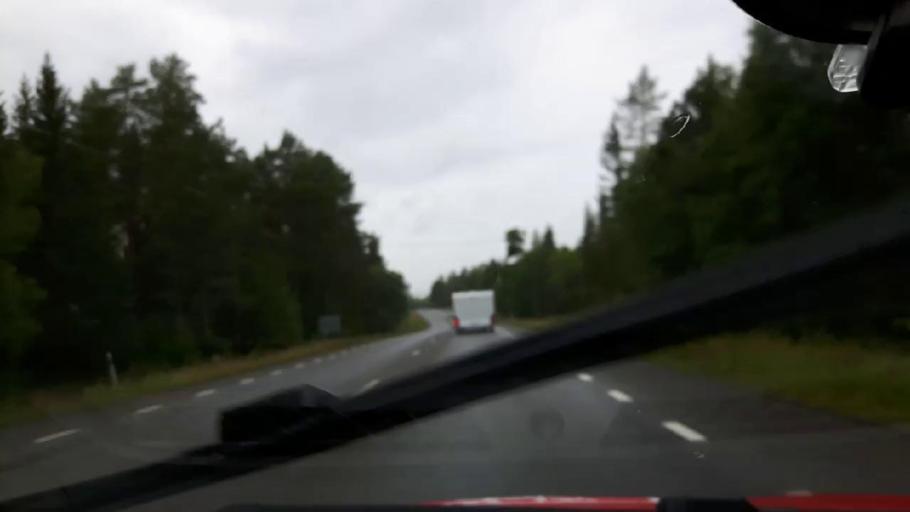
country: SE
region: Jaemtland
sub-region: Are Kommun
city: Jarpen
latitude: 63.3181
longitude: 13.5725
